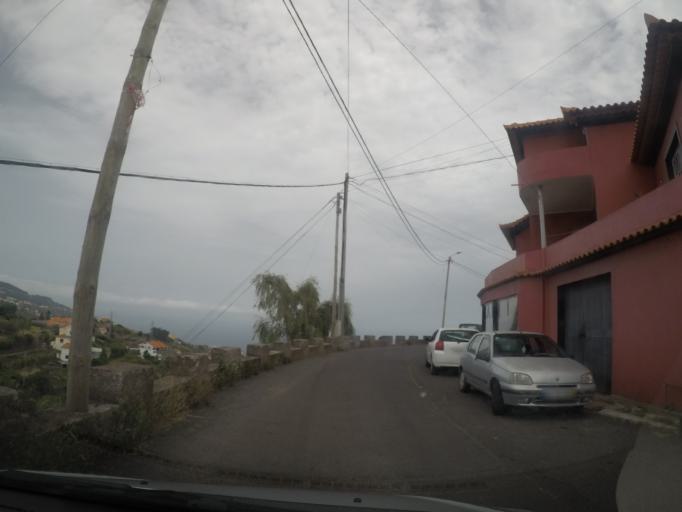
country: PT
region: Madeira
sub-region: Santa Cruz
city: Santa Cruz
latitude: 32.6878
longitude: -16.8139
